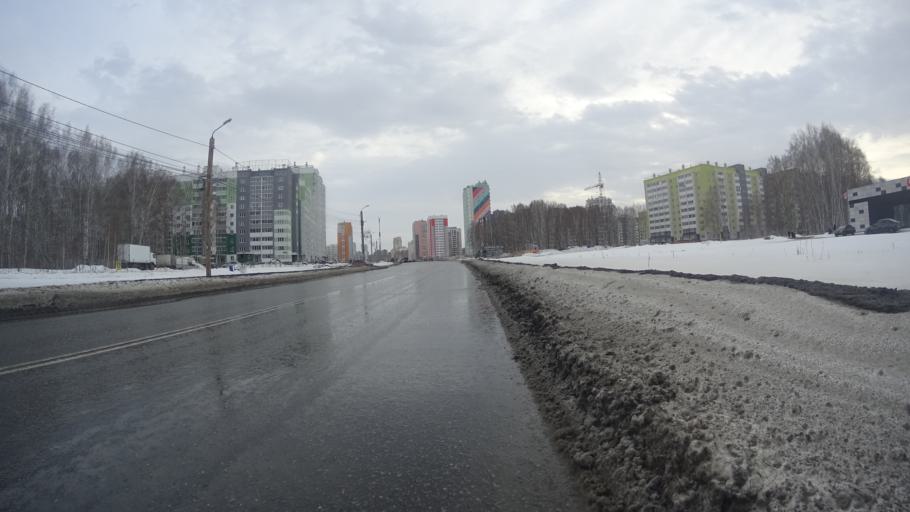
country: RU
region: Chelyabinsk
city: Roshchino
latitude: 55.2137
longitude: 61.2846
